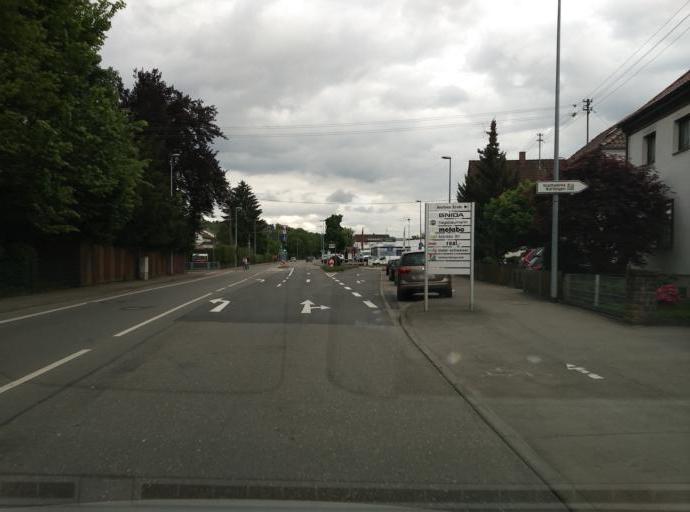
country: DE
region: Baden-Wuerttemberg
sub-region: Regierungsbezirk Stuttgart
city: Nurtingen
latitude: 48.6161
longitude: 9.3468
